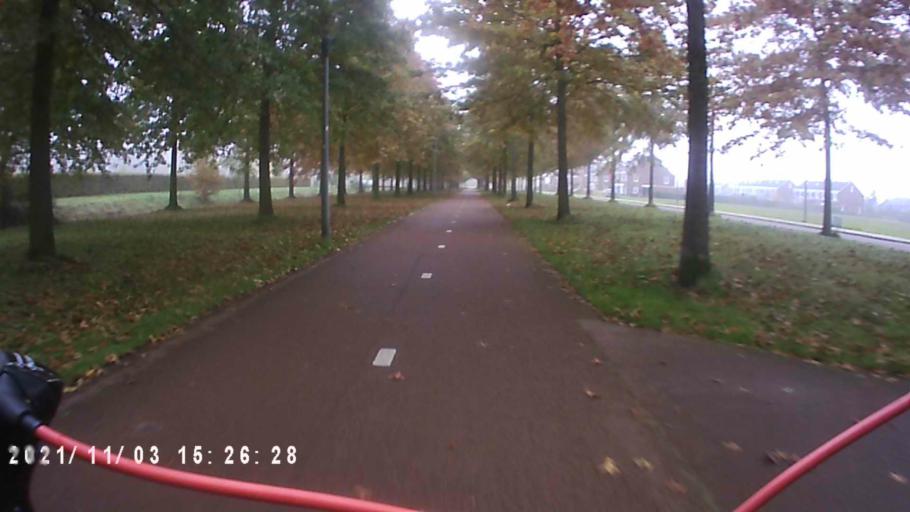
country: NL
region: Groningen
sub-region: Gemeente Leek
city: Leek
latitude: 53.1442
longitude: 6.3744
